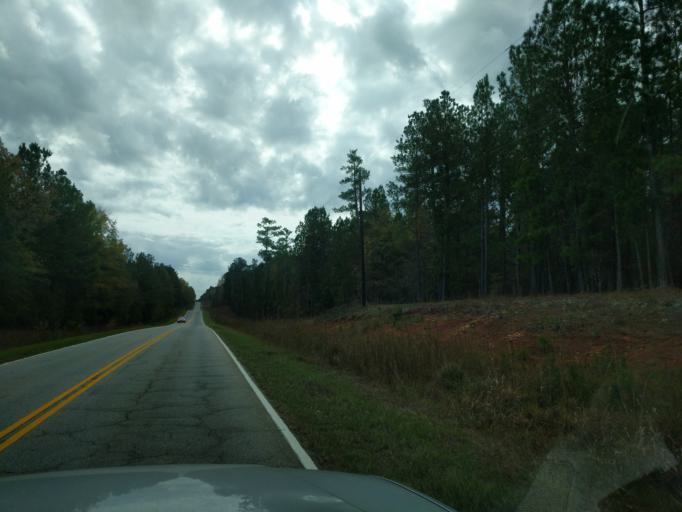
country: US
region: South Carolina
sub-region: Saluda County
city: Saluda
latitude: 34.1468
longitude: -81.8469
